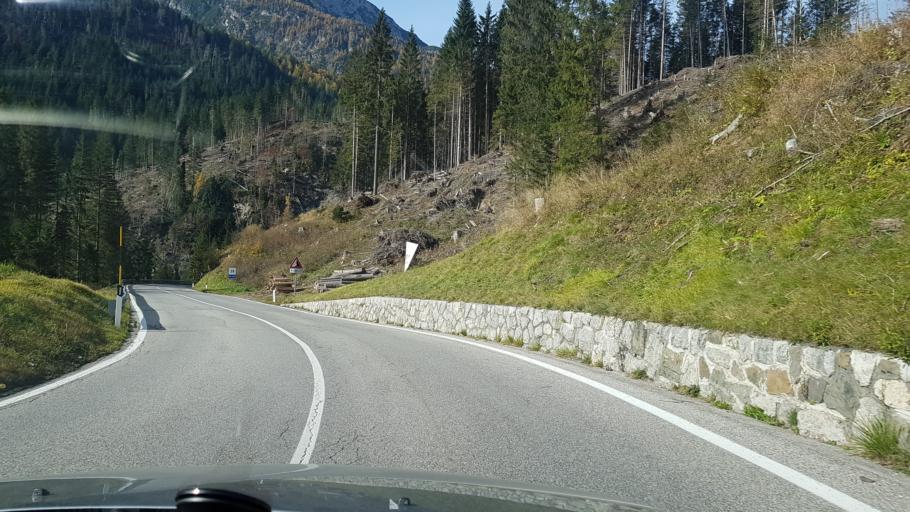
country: IT
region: Veneto
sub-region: Provincia di Belluno
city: Sappada
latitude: 46.5669
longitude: 12.6637
